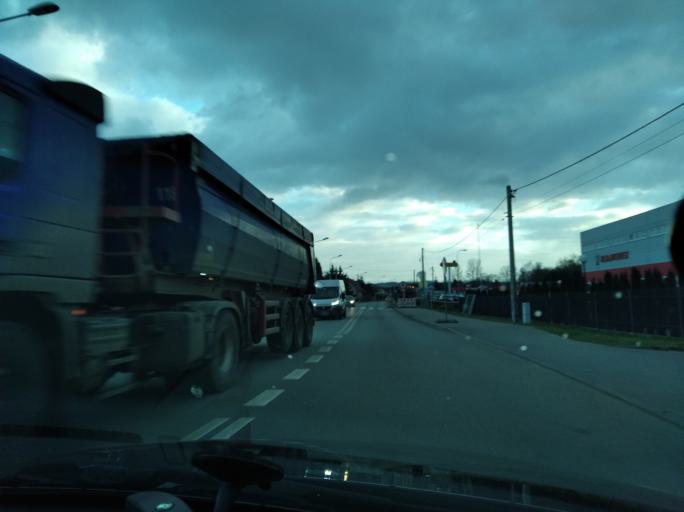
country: PL
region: Subcarpathian Voivodeship
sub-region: Rzeszow
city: Rzeszow
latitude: 50.0302
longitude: 22.0417
